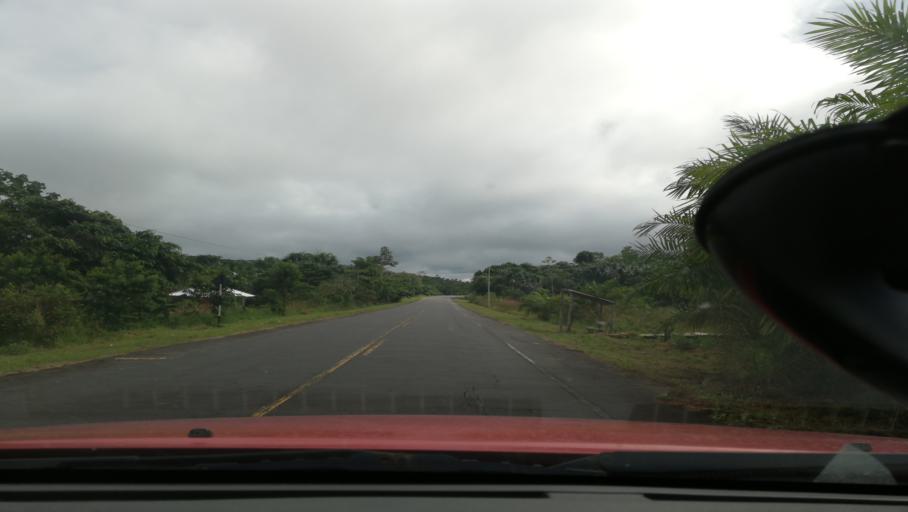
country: PE
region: Loreto
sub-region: Provincia de Loreto
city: Nauta
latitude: -4.2919
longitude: -73.5174
